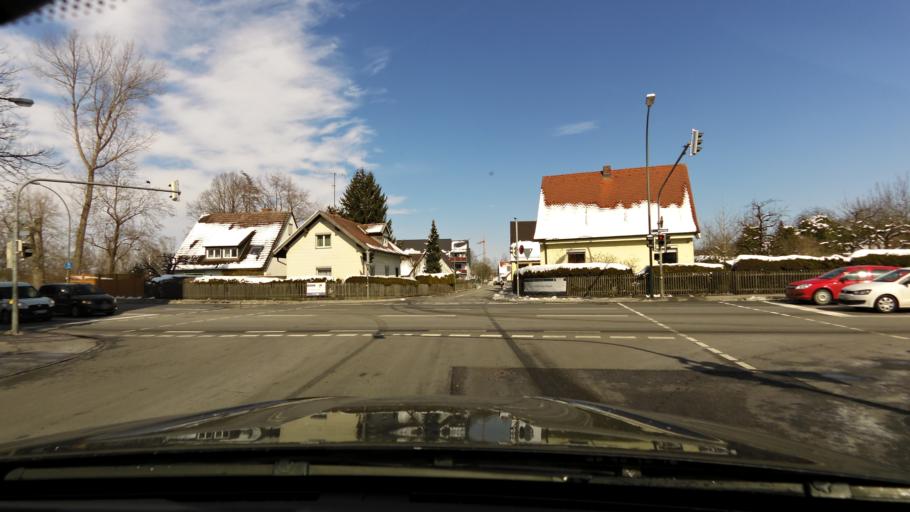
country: DE
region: Bavaria
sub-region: Lower Bavaria
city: Landshut
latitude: 48.5469
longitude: 12.1768
